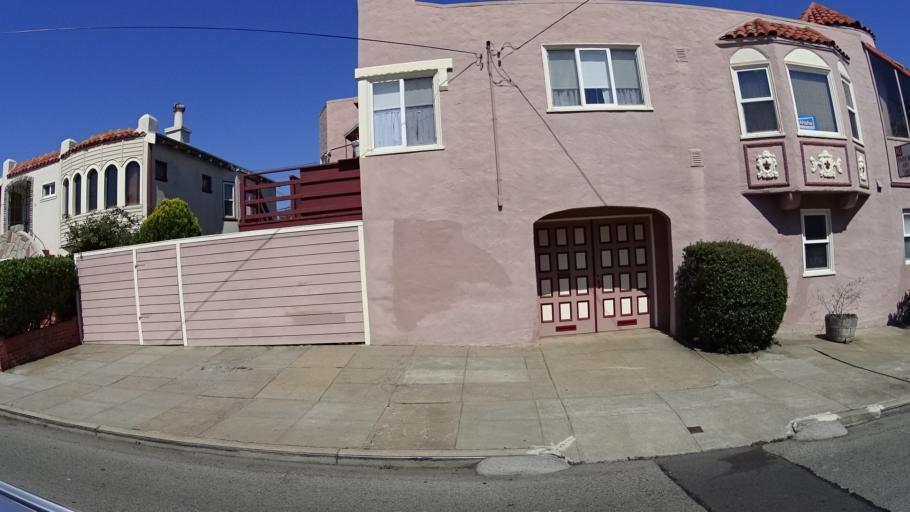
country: US
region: California
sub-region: San Mateo County
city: Daly City
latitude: 37.7276
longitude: -122.4414
